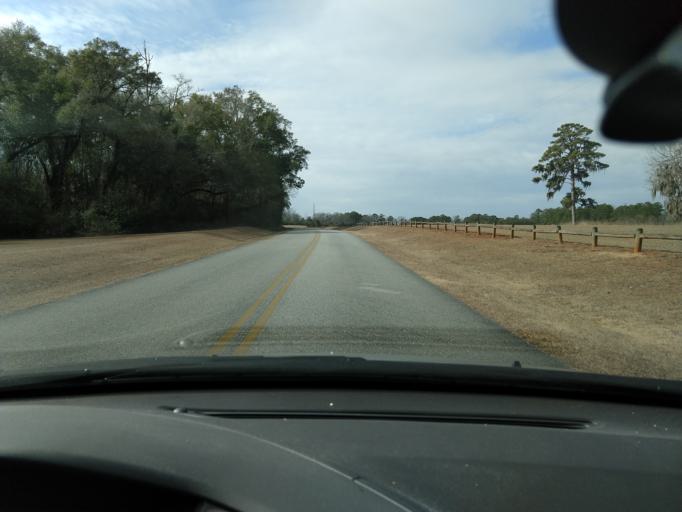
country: US
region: Georgia
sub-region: Early County
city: Blakely
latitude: 31.4683
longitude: -84.9388
